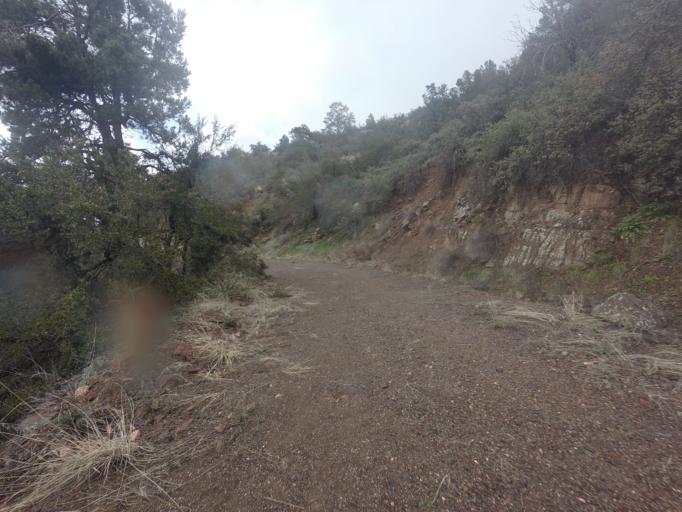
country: US
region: Arizona
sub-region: Gila County
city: Pine
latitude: 34.4027
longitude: -111.5961
